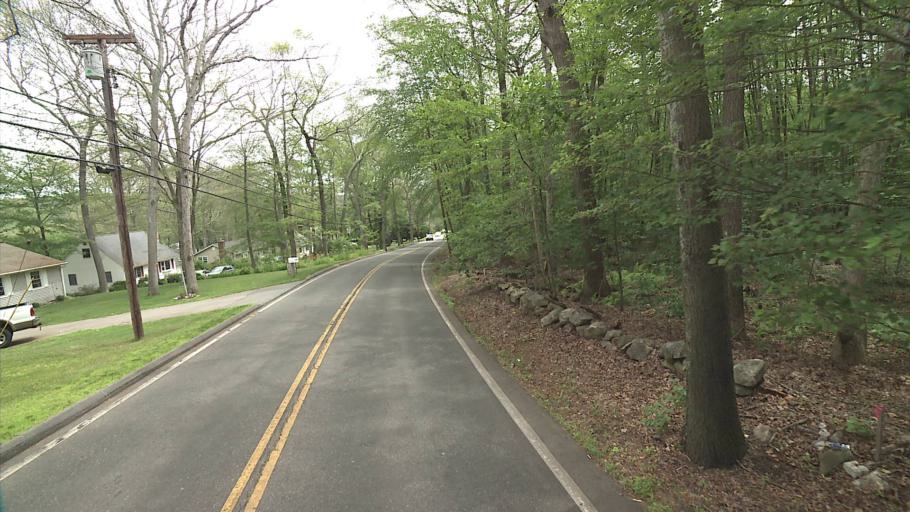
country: US
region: Connecticut
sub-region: New London County
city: Ledyard Center
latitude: 41.4467
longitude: -72.0151
